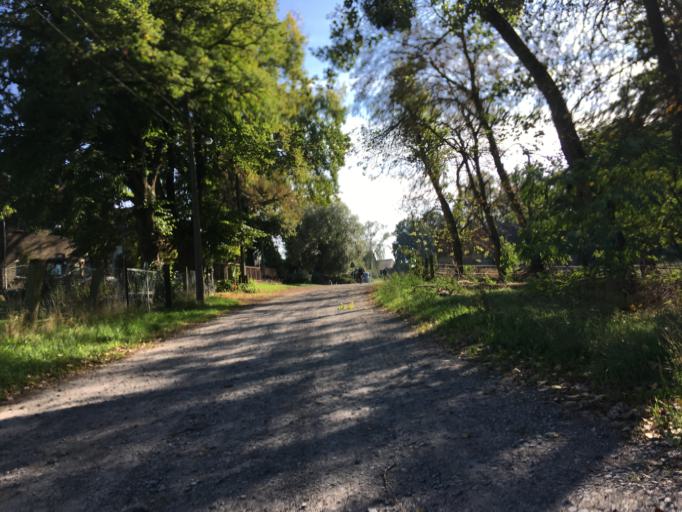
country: DE
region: Brandenburg
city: Altlandsberg
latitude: 52.5339
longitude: 13.7228
